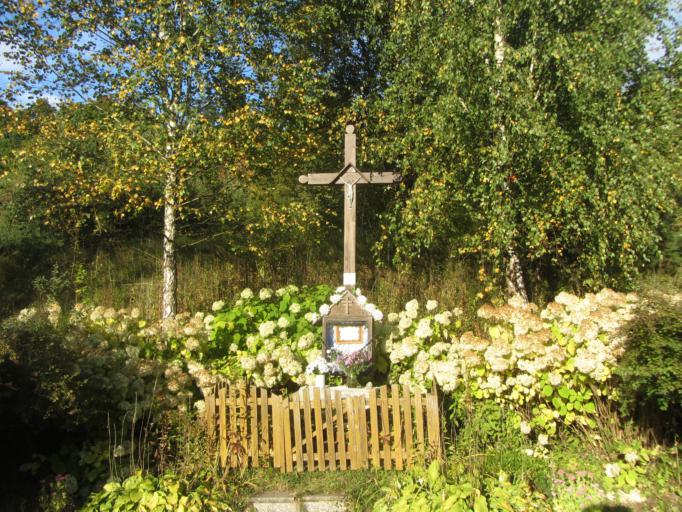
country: LT
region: Vilnius County
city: Lazdynai
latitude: 54.6401
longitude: 25.2114
